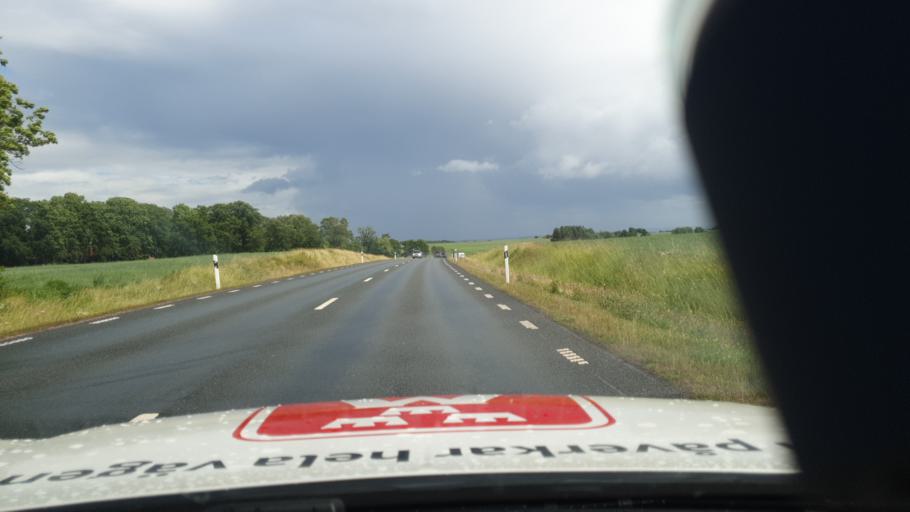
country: SE
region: Vaestra Goetaland
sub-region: Falkopings Kommun
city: Akarp
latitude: 58.1268
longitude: 13.7883
